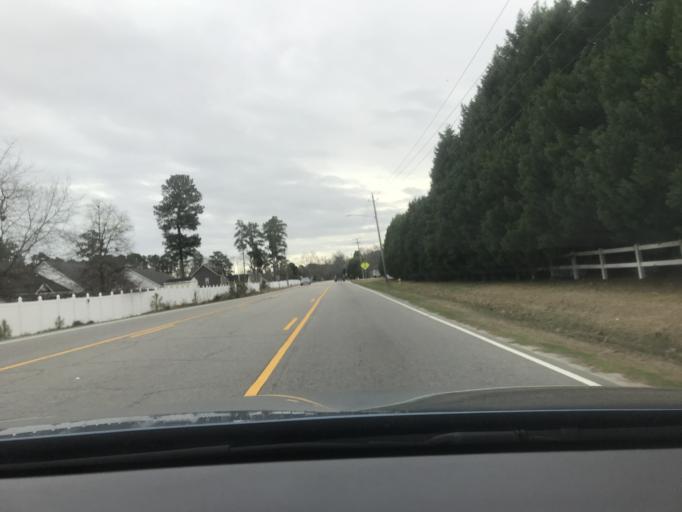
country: US
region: North Carolina
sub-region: Hoke County
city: Rockfish
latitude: 35.0444
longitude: -79.0078
